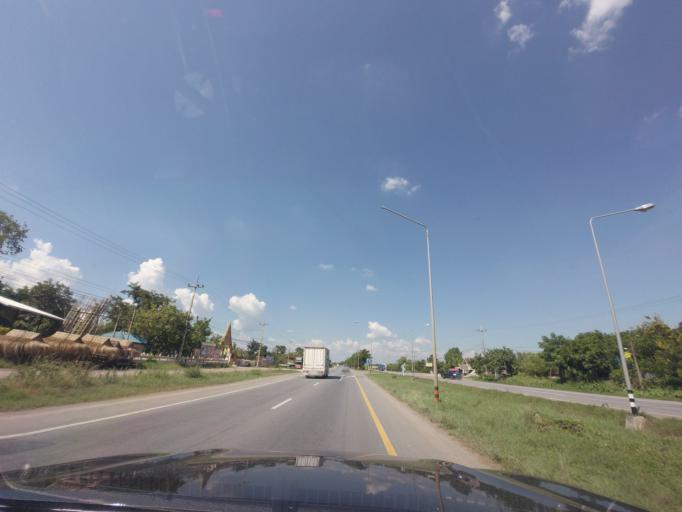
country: TH
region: Nakhon Ratchasima
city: Non Sung
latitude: 15.1690
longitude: 102.3343
